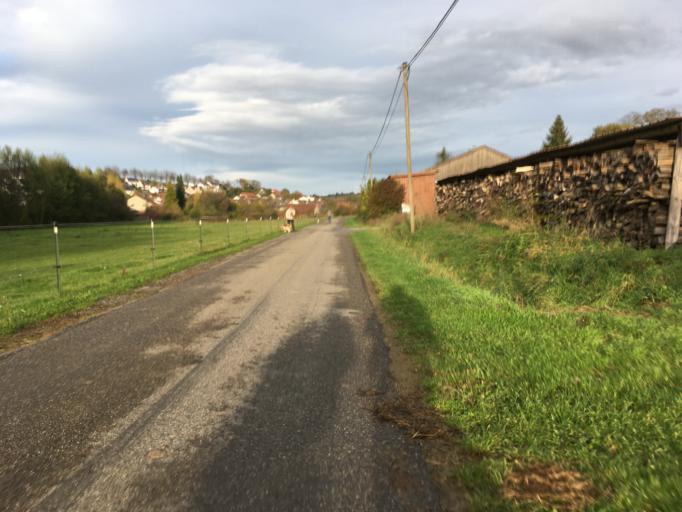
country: DE
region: Baden-Wuerttemberg
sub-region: Regierungsbezirk Stuttgart
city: Jagsthausen
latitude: 49.3617
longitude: 9.4809
